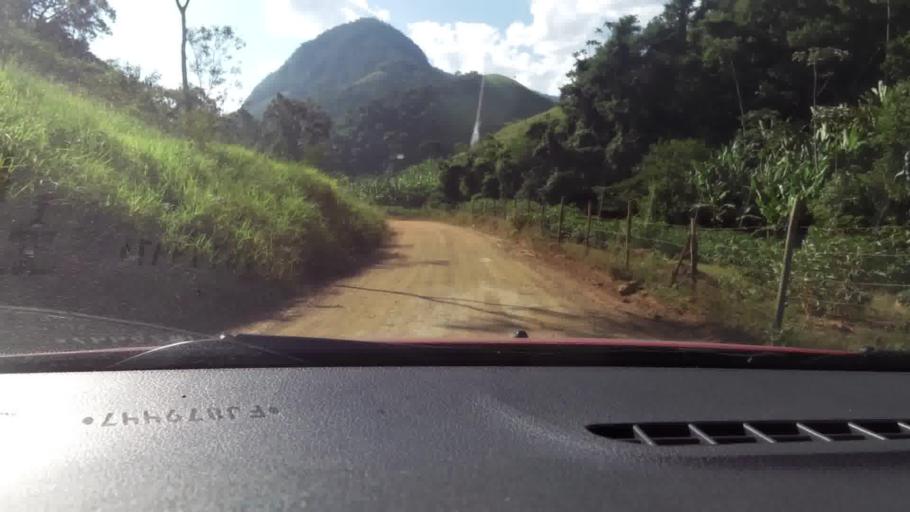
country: BR
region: Espirito Santo
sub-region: Guarapari
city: Guarapari
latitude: -20.5263
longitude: -40.5651
